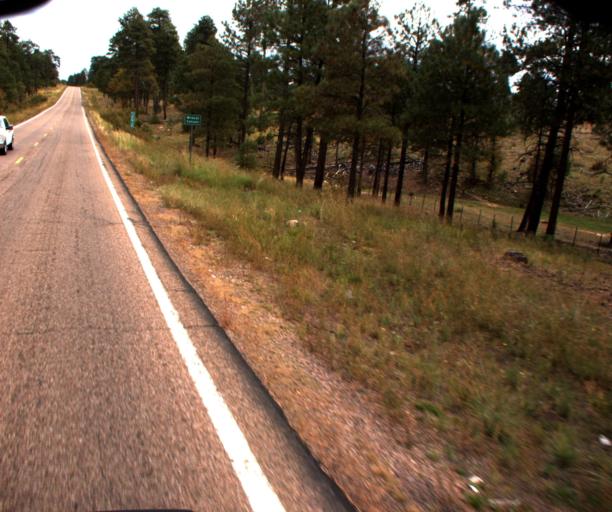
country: US
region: Arizona
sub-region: Navajo County
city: Heber-Overgaard
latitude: 34.3365
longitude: -110.7393
